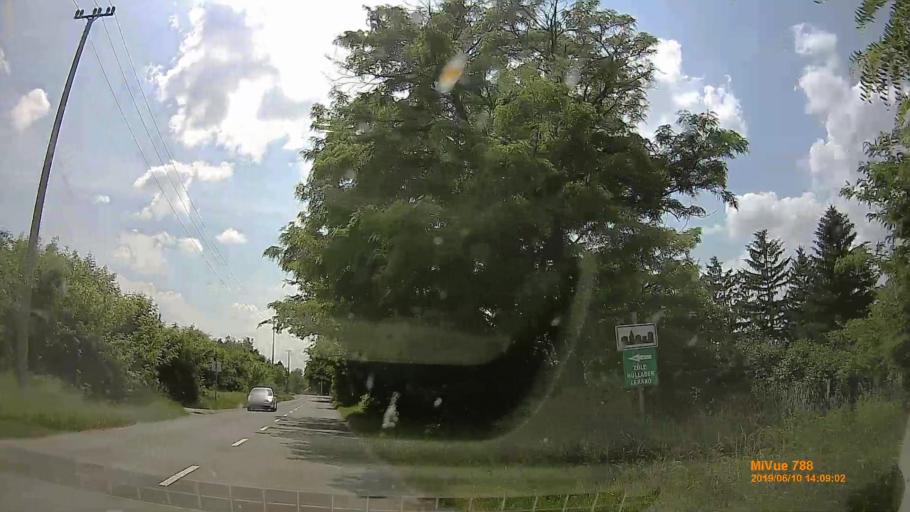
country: HU
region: Pest
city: God
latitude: 47.6839
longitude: 19.1546
